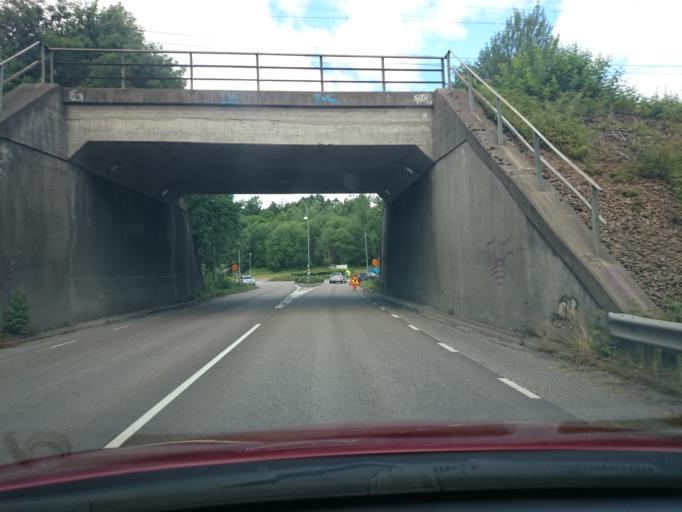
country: SE
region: Vaestra Goetaland
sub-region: Lerums Kommun
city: Lerum
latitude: 57.7770
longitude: 12.2860
